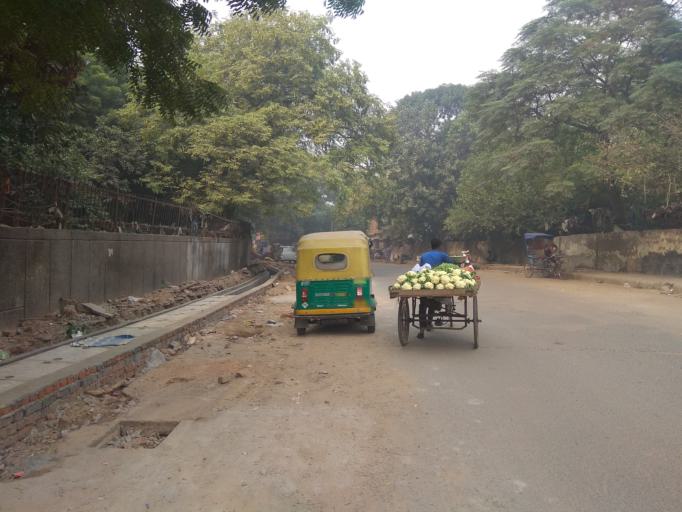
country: IN
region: NCT
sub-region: New Delhi
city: New Delhi
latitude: 28.5698
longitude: 77.2453
